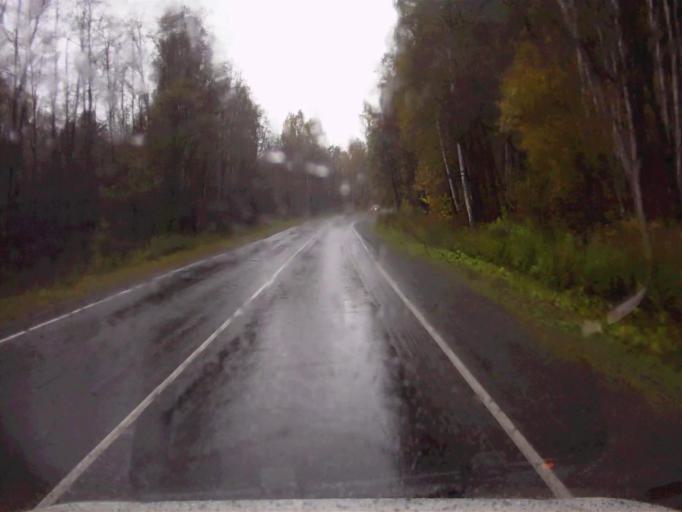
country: RU
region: Chelyabinsk
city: Kyshtym
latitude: 55.9061
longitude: 60.4415
